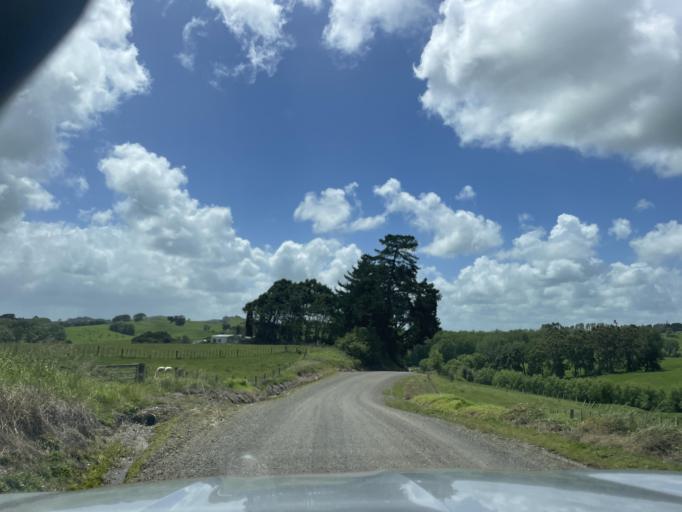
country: NZ
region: Auckland
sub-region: Auckland
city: Wellsford
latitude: -36.1801
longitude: 174.3155
